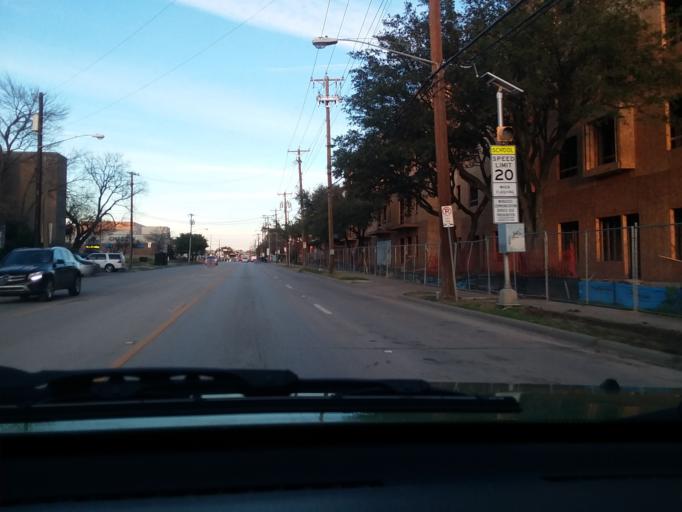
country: US
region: Texas
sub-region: Dallas County
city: Highland Park
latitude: 32.8041
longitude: -96.7787
